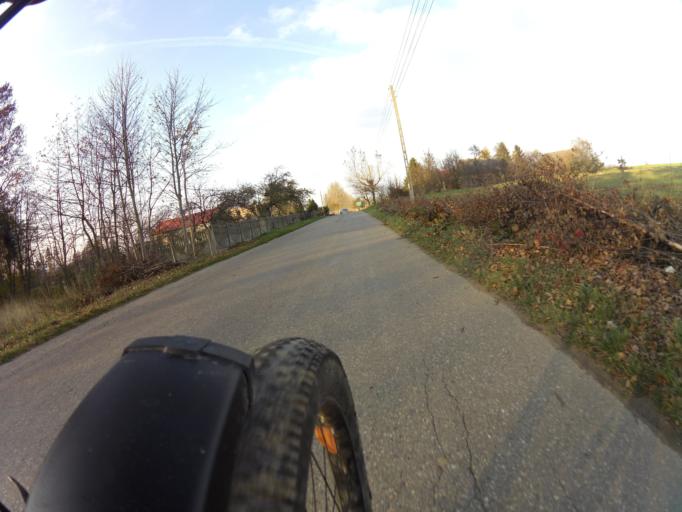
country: PL
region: Pomeranian Voivodeship
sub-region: Powiat pucki
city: Krokowa
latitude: 54.7674
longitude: 18.1800
